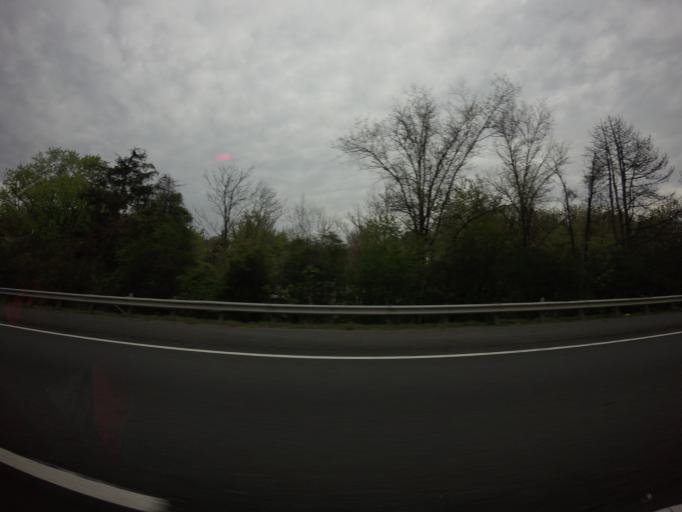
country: US
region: Maryland
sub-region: Carroll County
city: Mount Airy
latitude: 39.3653
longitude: -77.1850
